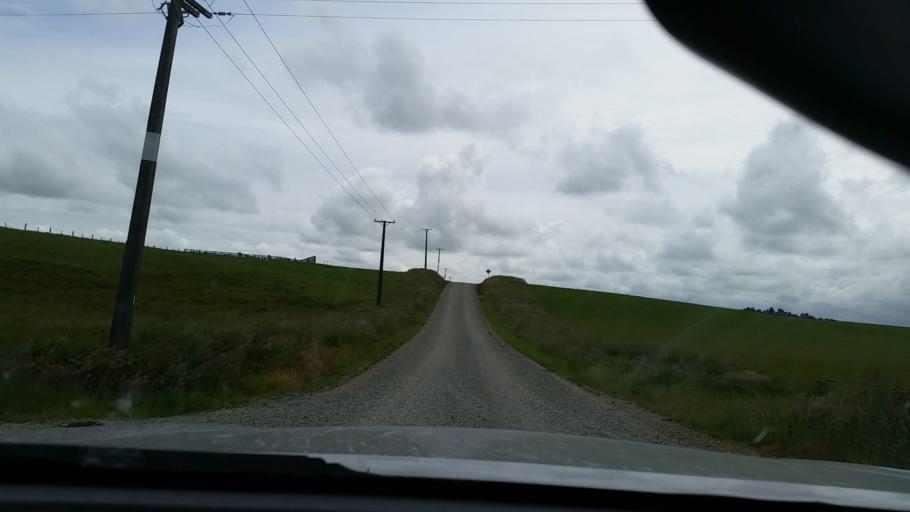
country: NZ
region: Southland
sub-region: Southland District
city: Winton
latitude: -46.2269
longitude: 168.2618
